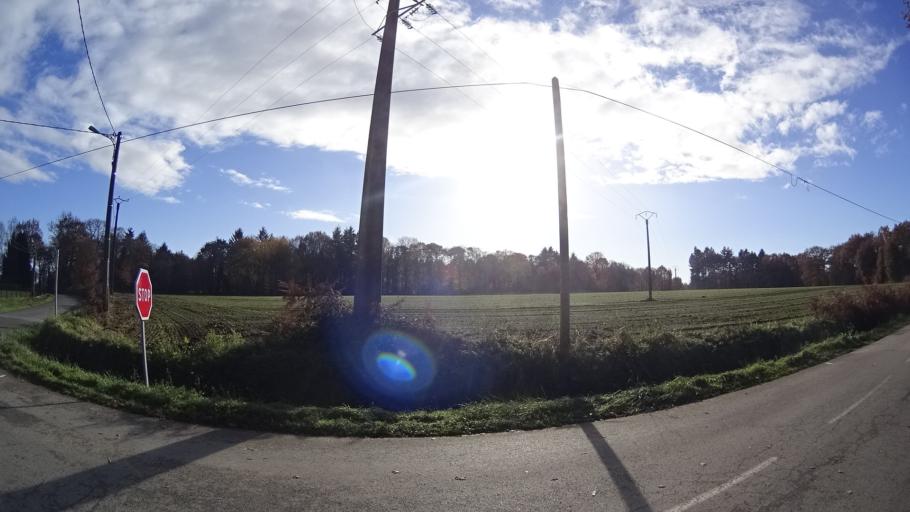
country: FR
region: Brittany
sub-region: Departement du Morbihan
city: La Gacilly
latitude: 47.7882
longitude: -2.1566
